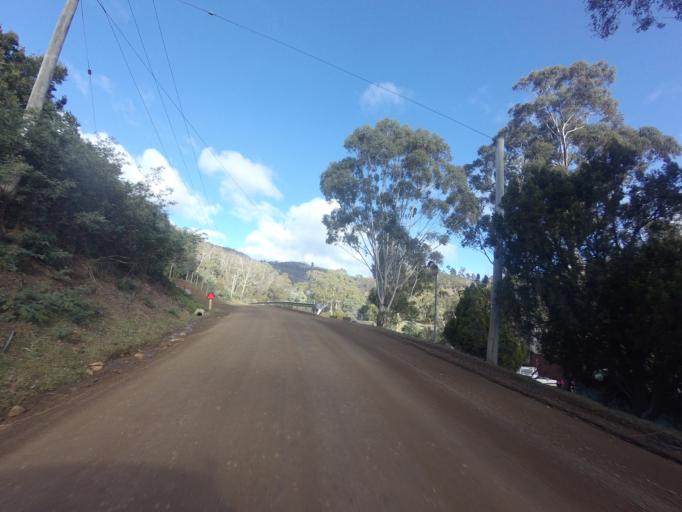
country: AU
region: Tasmania
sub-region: Derwent Valley
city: New Norfolk
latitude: -42.8140
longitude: 147.1300
